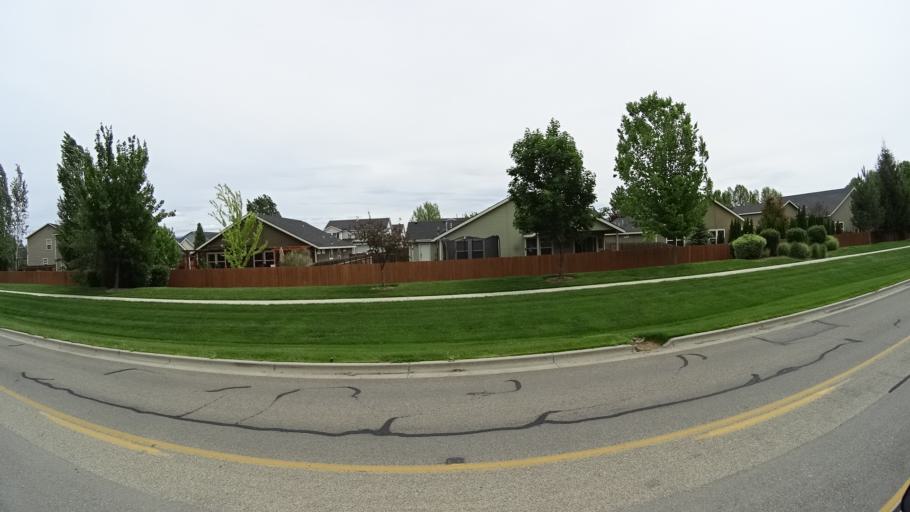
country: US
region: Idaho
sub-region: Ada County
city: Meridian
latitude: 43.5637
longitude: -116.3745
